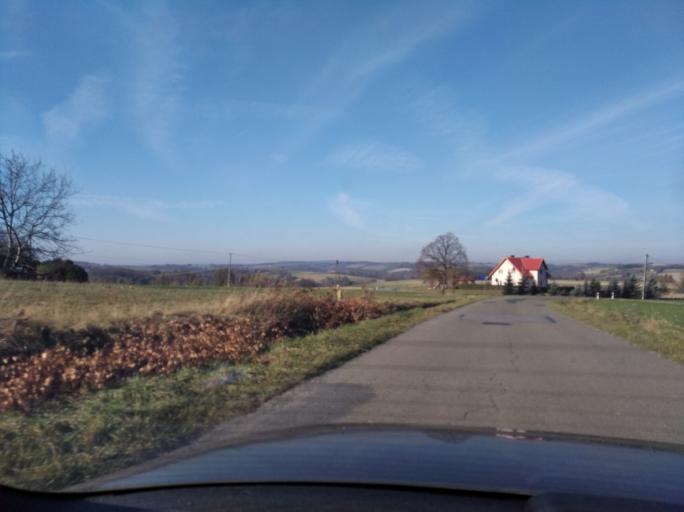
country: PL
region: Subcarpathian Voivodeship
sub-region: Powiat ropczycko-sedziszowski
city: Wielopole Skrzynskie
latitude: 49.9193
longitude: 21.5637
